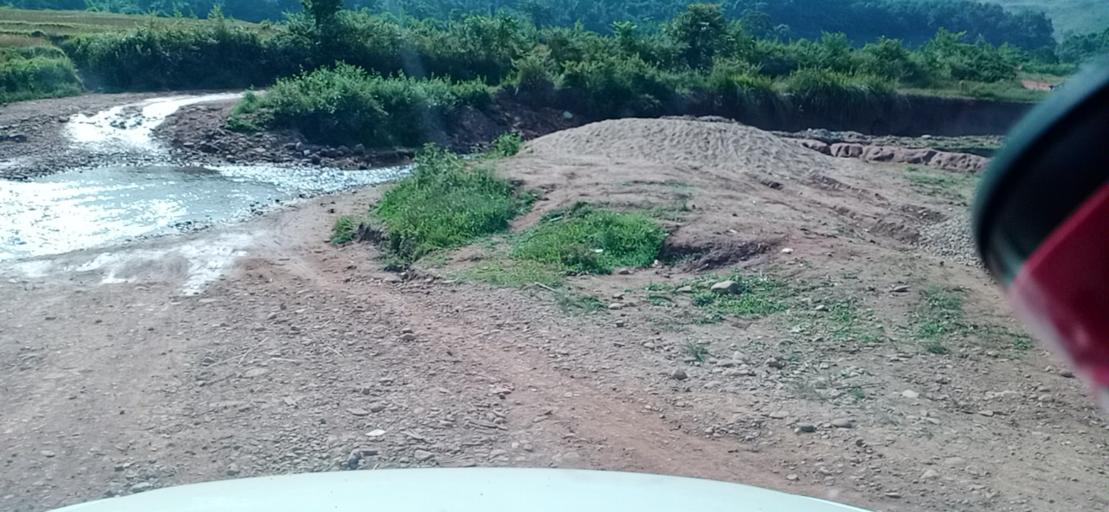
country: TH
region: Changwat Bueng Kan
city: Pak Khat
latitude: 18.6757
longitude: 103.1947
